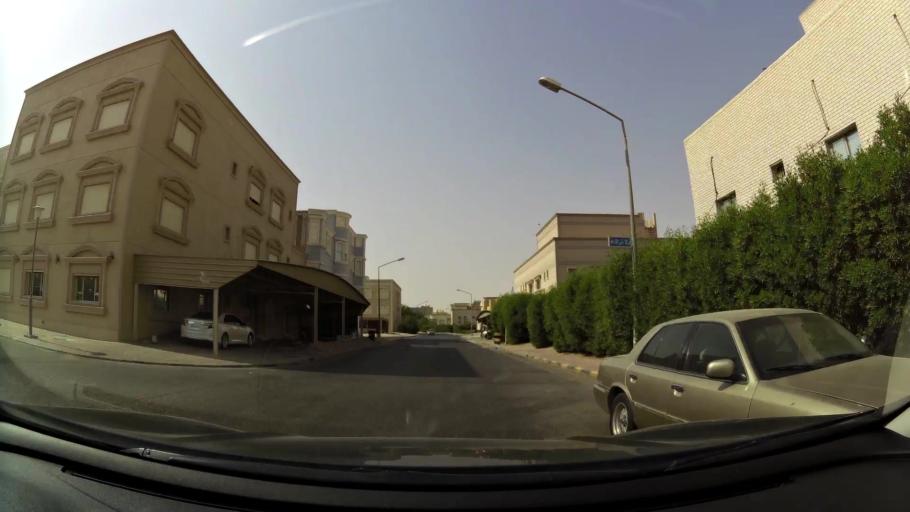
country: KW
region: Muhafazat al Jahra'
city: Al Jahra'
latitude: 29.3243
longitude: 47.6680
